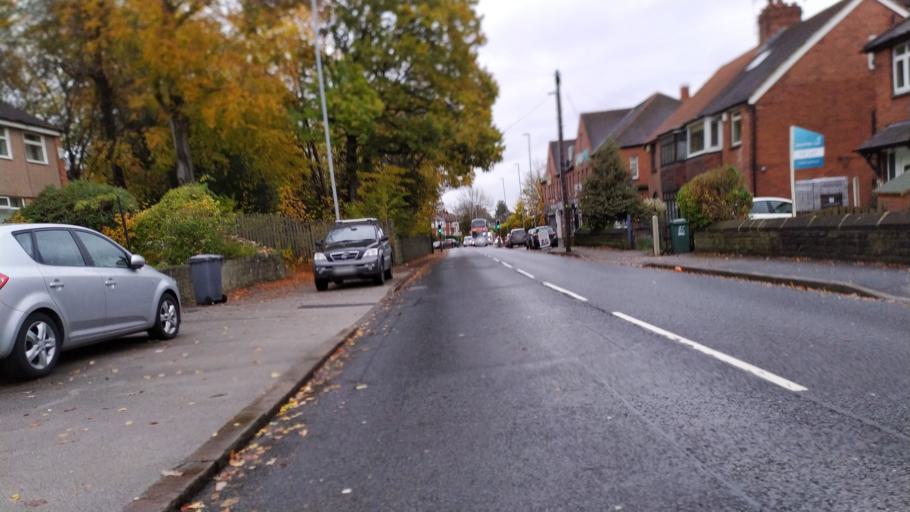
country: GB
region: England
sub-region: City and Borough of Leeds
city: Leeds
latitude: 53.8137
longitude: -1.5900
